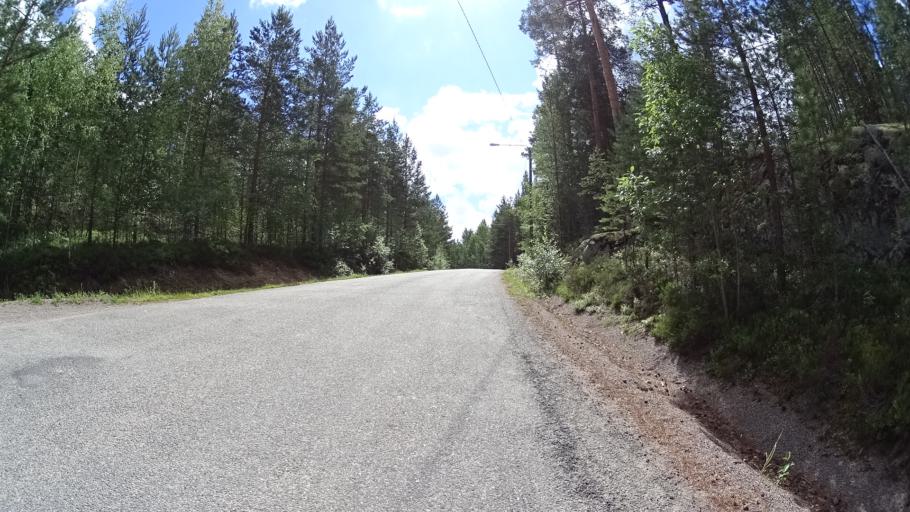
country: FI
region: Uusimaa
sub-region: Helsinki
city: Espoo
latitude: 60.3587
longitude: 24.6656
